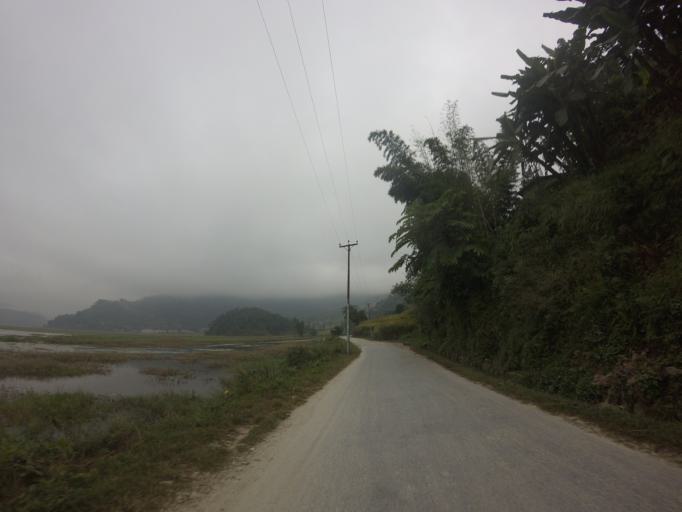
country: NP
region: Western Region
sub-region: Gandaki Zone
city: Pokhara
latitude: 28.2285
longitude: 83.9325
